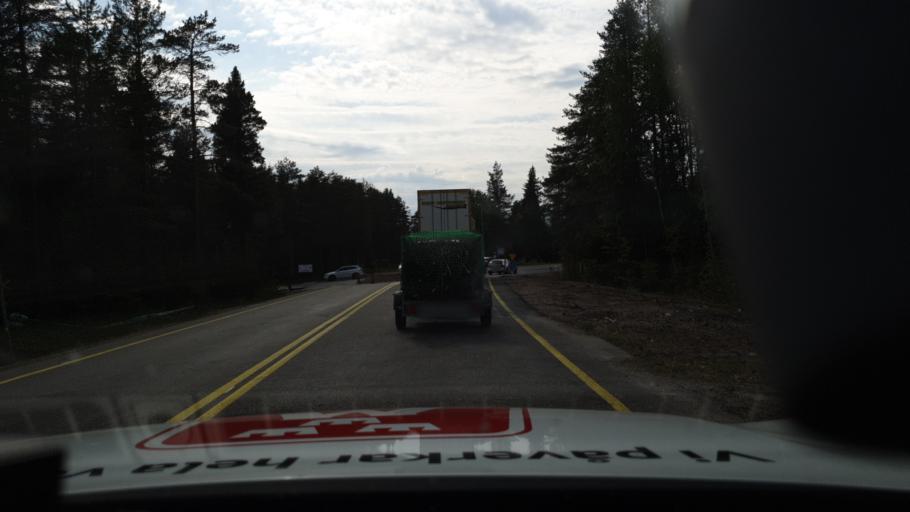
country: SE
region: Norrbotten
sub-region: Lulea Kommun
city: Ranea
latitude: 65.8643
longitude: 22.3100
